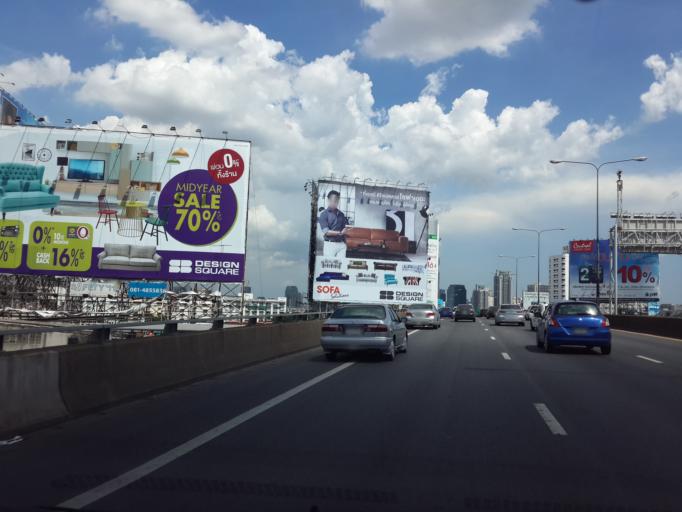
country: TH
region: Bangkok
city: Din Daeng
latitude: 13.7618
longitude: 100.5454
